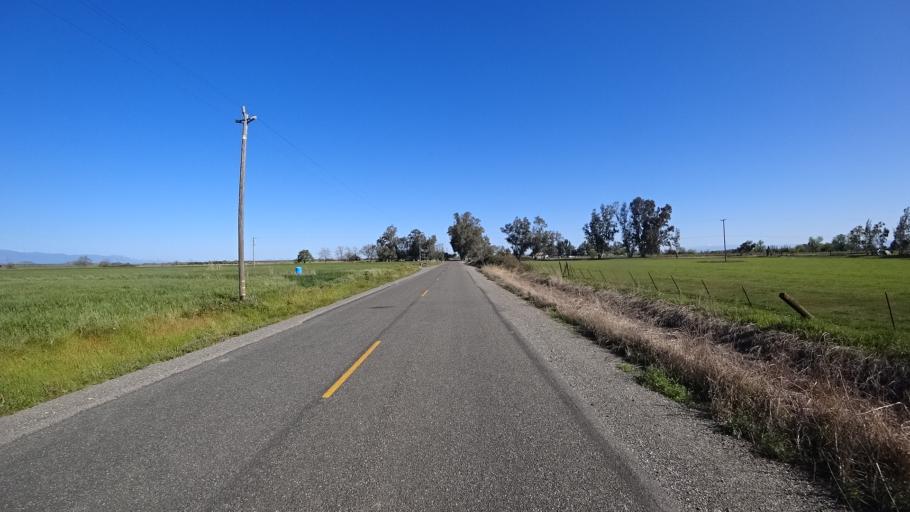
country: US
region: California
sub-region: Glenn County
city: Orland
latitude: 39.7531
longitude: -122.2480
